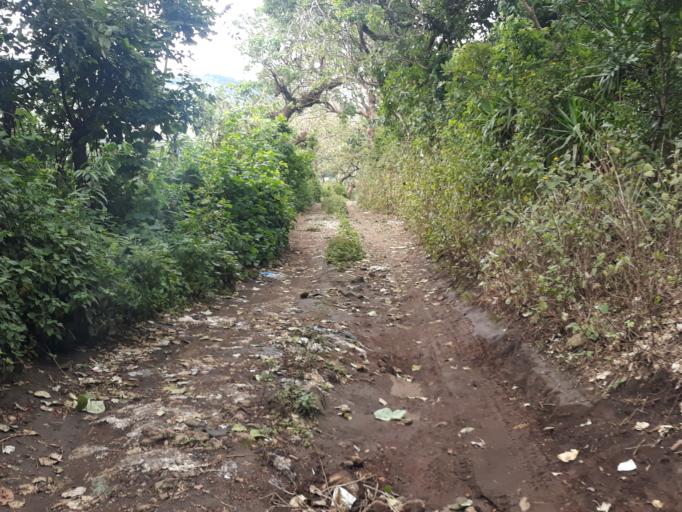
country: GT
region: Escuintla
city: San Vicente Pacaya
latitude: 14.3698
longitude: -90.5540
